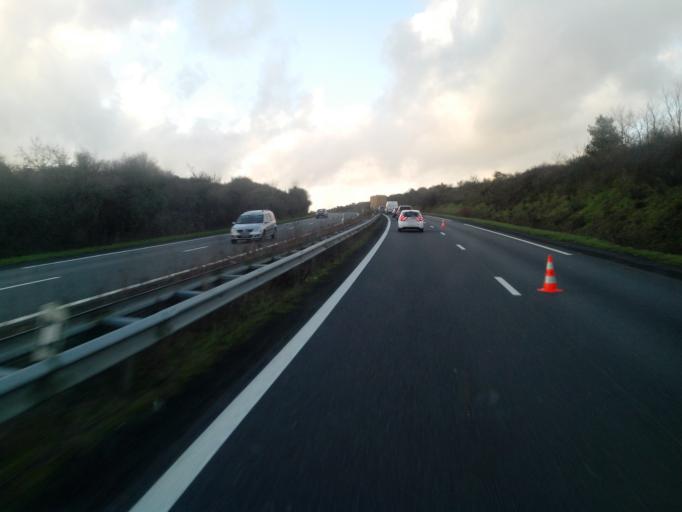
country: FR
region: Pays de la Loire
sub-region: Departement de la Loire-Atlantique
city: La Regrippiere
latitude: 47.1531
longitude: -1.2001
